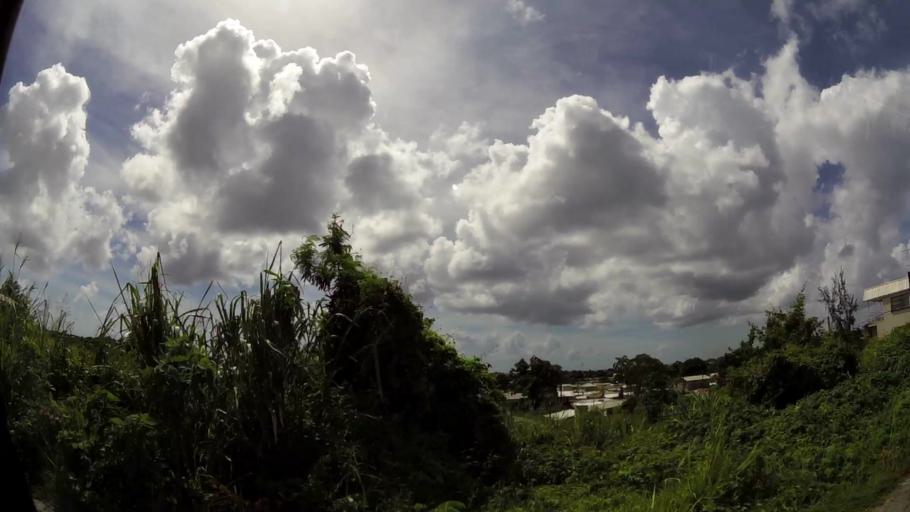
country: BB
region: Saint Michael
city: Bridgetown
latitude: 13.1271
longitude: -59.6172
